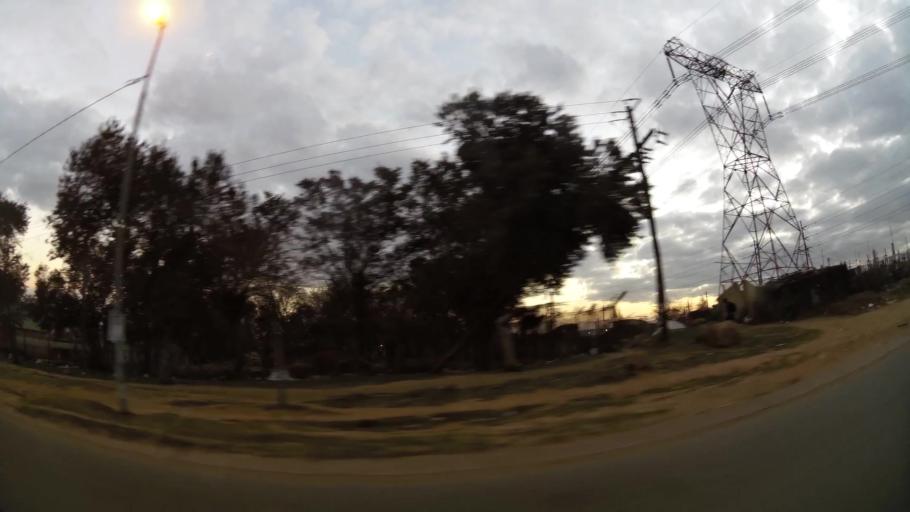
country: ZA
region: Gauteng
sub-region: Ekurhuleni Metropolitan Municipality
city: Tembisa
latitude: -25.9986
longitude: 28.1894
